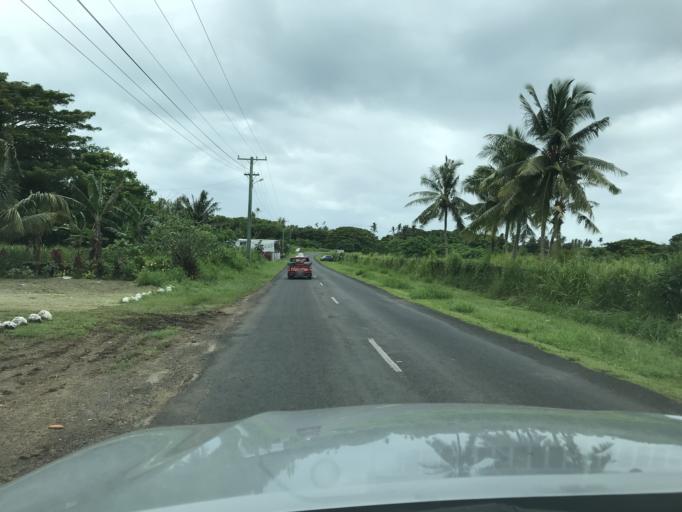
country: WS
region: Aiga-i-le-Tai
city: Mulifanua
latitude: -13.8325
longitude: -172.0285
